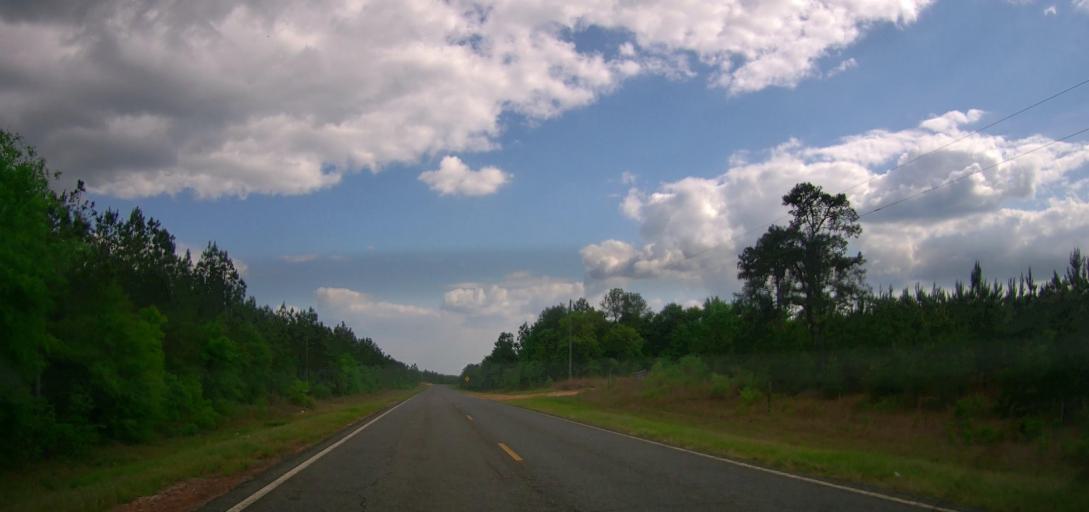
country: US
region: Georgia
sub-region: Johnson County
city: Wrightsville
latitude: 32.7572
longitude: -82.9284
